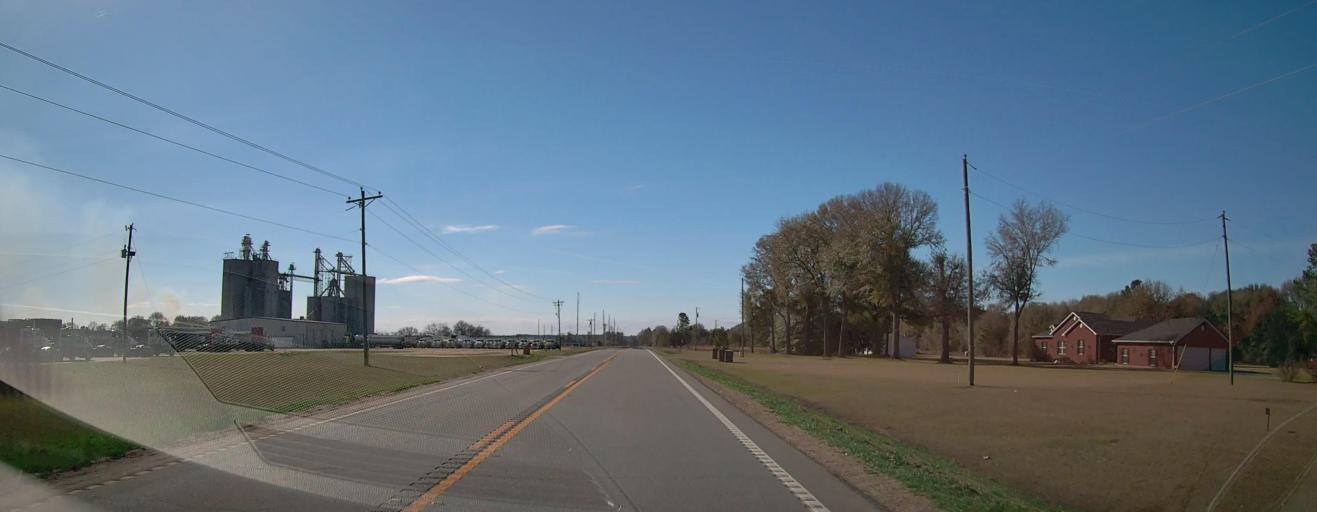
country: US
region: Georgia
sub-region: Macon County
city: Oglethorpe
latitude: 32.3334
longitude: -84.1087
